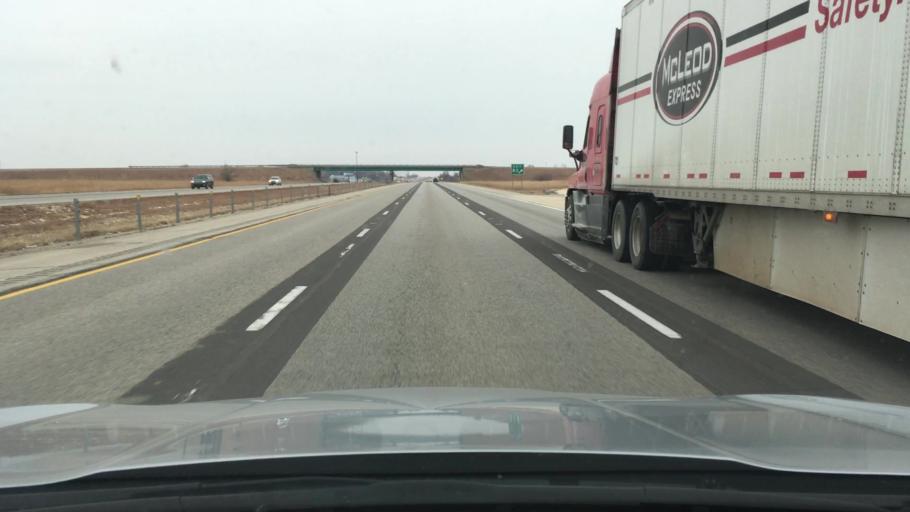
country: US
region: Illinois
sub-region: Sangamon County
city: Divernon
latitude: 39.6130
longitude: -89.6467
